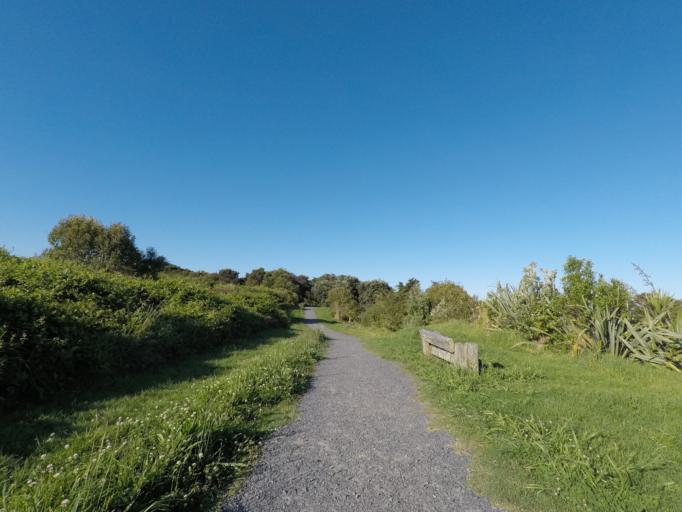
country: NZ
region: Auckland
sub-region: Auckland
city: Rosebank
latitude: -36.8413
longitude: 174.6592
